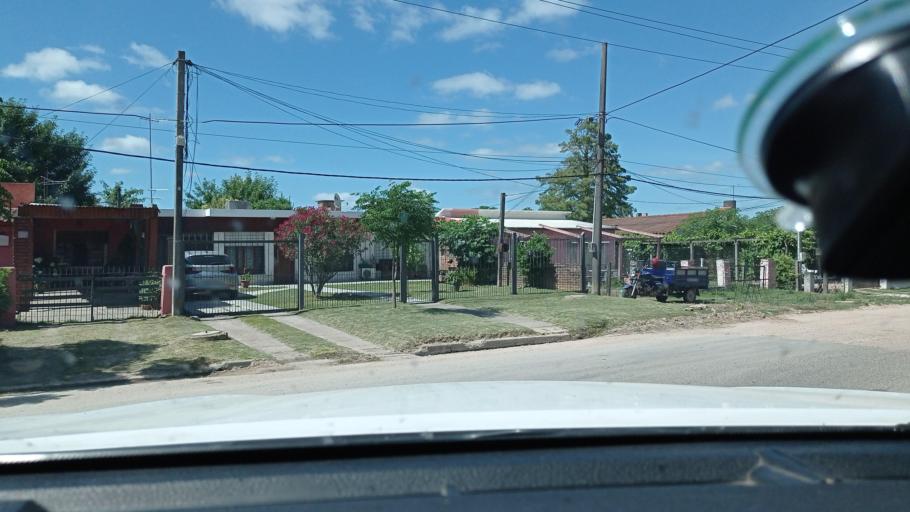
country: UY
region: Canelones
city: Pando
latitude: -34.7176
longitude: -55.9693
